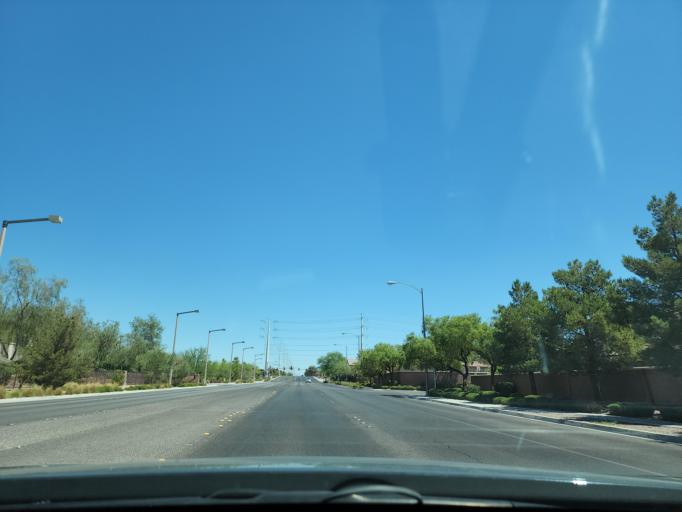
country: US
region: Nevada
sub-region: Clark County
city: Summerlin South
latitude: 36.0826
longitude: -115.3155
